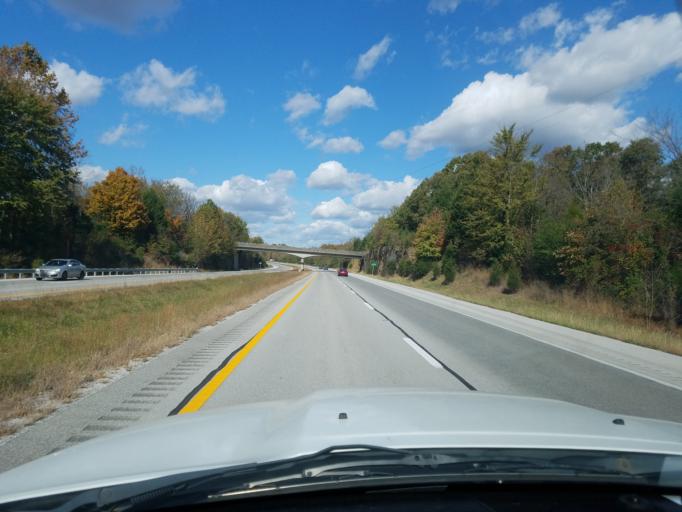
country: US
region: Kentucky
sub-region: Butler County
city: Morgantown
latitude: 37.1734
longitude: -86.6669
